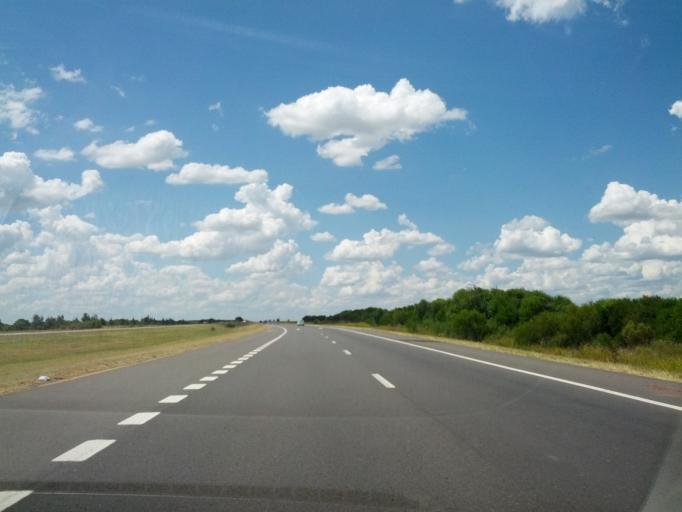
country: AR
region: Entre Rios
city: Colonia Elia
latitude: -32.7446
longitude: -58.4779
